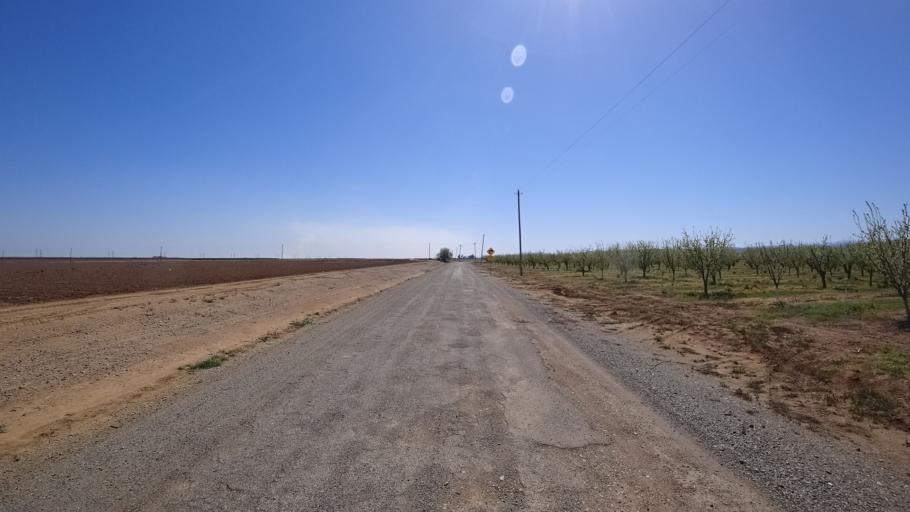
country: US
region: California
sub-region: Glenn County
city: Willows
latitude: 39.4821
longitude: -122.2772
